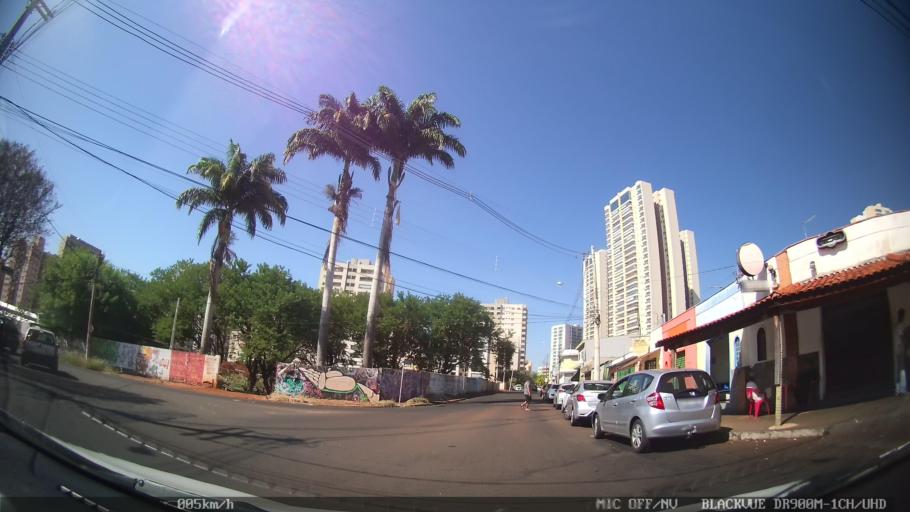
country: BR
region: Sao Paulo
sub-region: Ribeirao Preto
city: Ribeirao Preto
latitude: -21.2063
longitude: -47.7966
